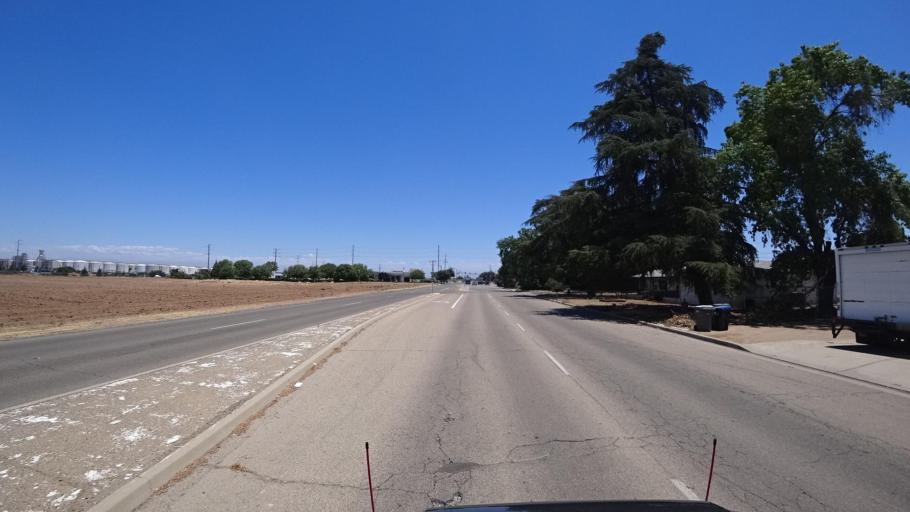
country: US
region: California
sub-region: Fresno County
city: Sunnyside
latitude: 36.7506
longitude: -119.7028
